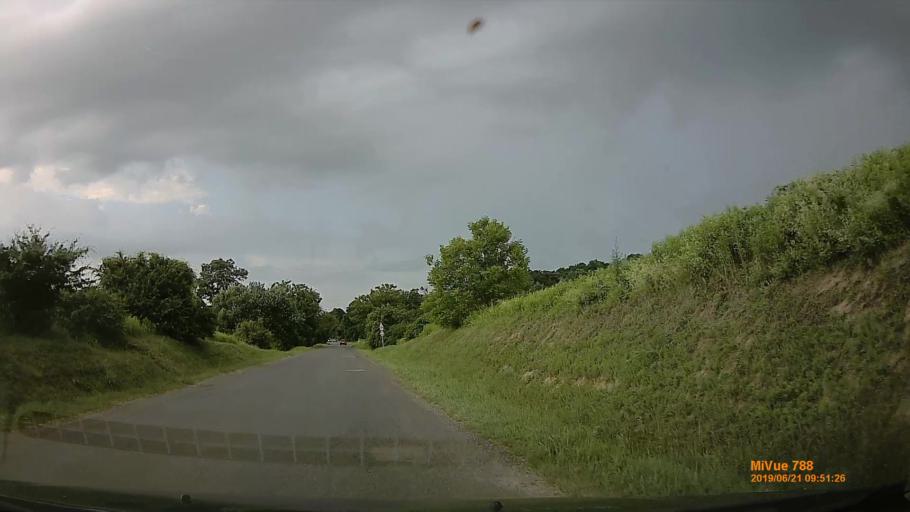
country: HU
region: Baranya
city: Sasd
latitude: 46.2520
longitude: 18.0222
